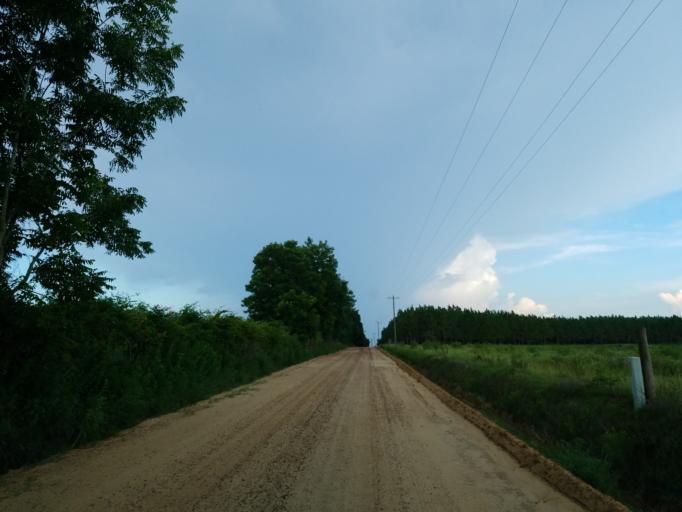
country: US
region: Georgia
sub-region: Tift County
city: Omega
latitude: 31.2753
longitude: -83.5262
